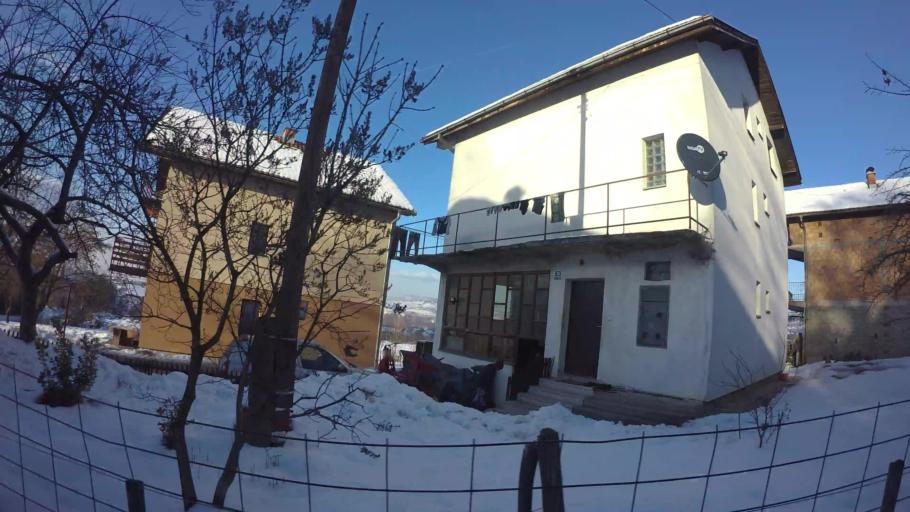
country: BA
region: Federation of Bosnia and Herzegovina
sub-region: Kanton Sarajevo
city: Sarajevo
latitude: 43.8087
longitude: 18.3512
